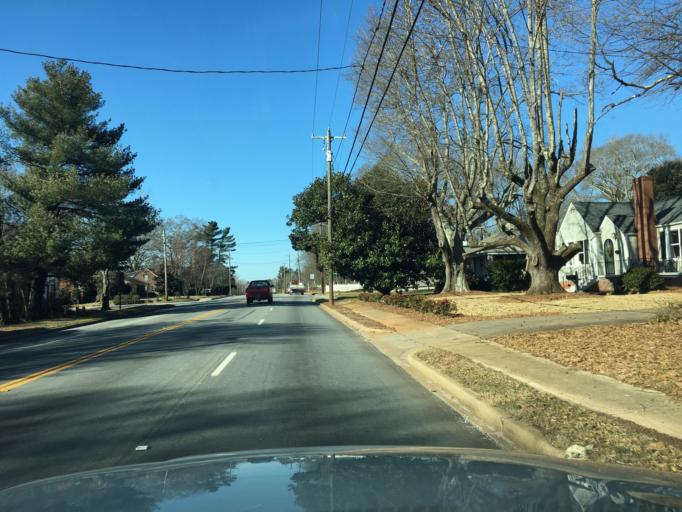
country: US
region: South Carolina
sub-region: Greenville County
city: Sans Souci
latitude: 34.8904
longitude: -82.4108
